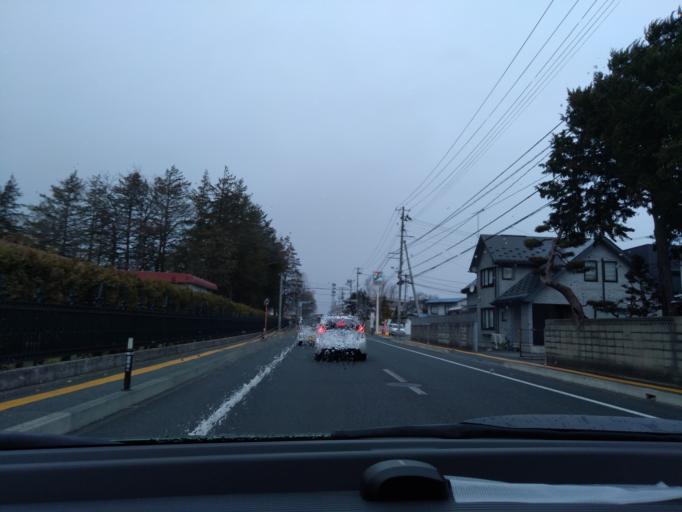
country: JP
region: Iwate
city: Morioka-shi
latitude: 39.7144
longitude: 141.1401
